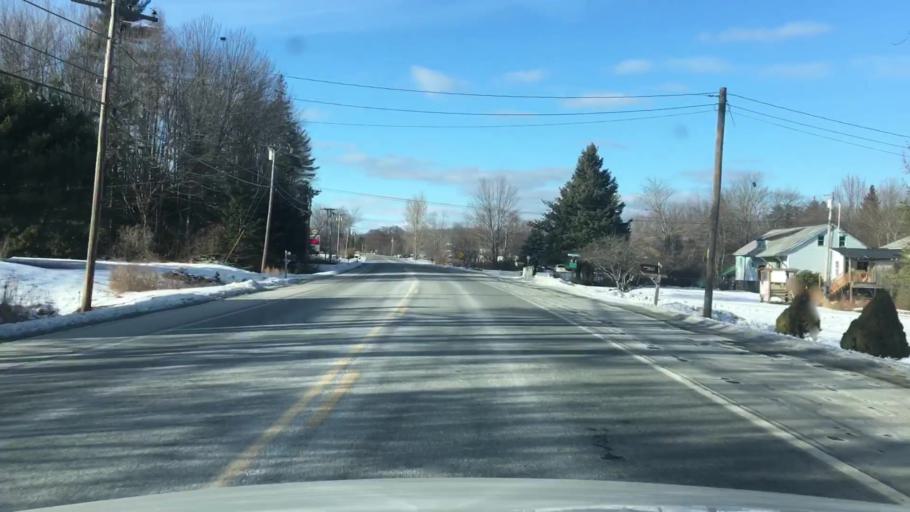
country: US
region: Maine
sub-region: Penobscot County
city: Eddington
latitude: 44.8223
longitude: -68.6502
